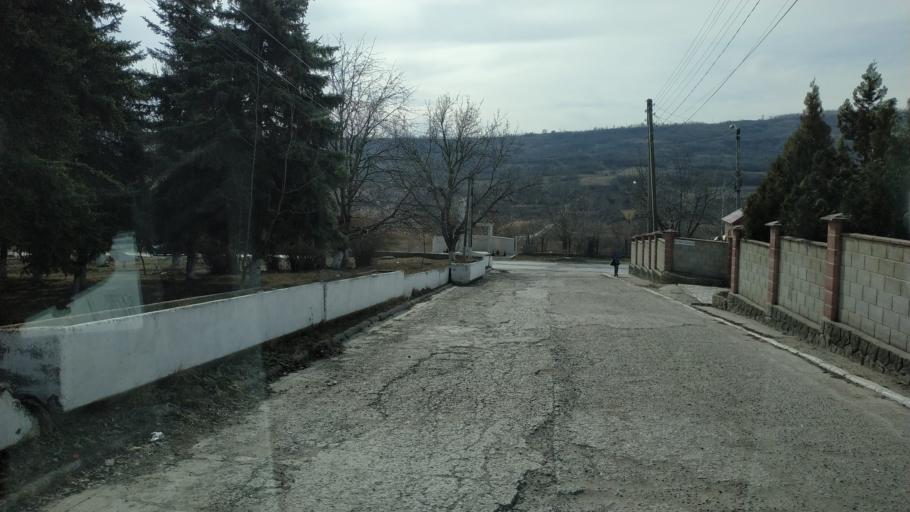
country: MD
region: Chisinau
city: Vatra
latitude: 47.0908
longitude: 28.6872
